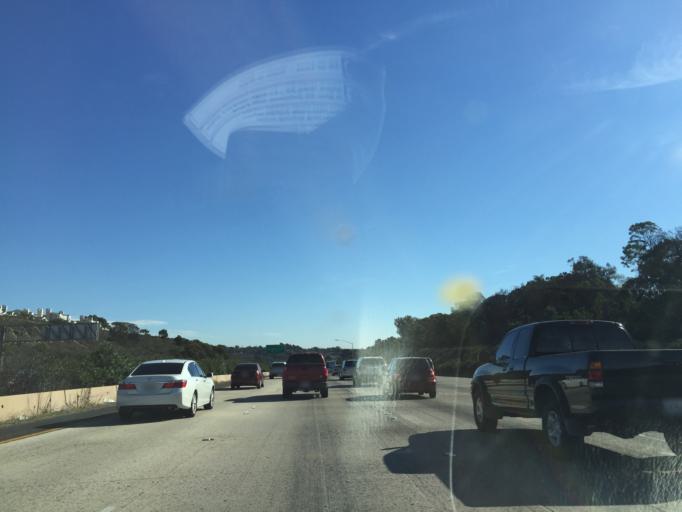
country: US
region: California
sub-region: San Diego County
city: Encinitas
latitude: 33.0980
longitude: -117.3072
